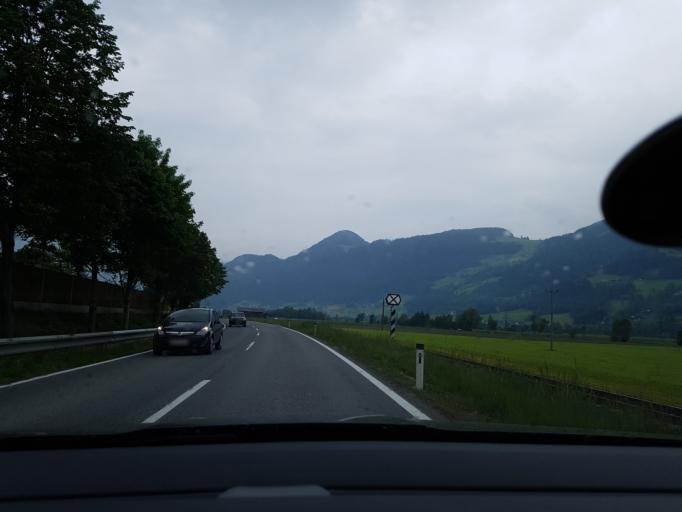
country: AT
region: Tyrol
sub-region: Politischer Bezirk Schwaz
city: Fugen
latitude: 47.3581
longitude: 11.8526
